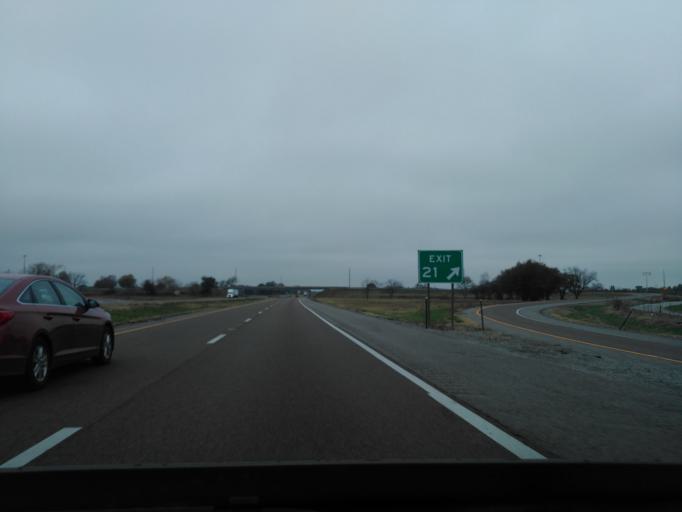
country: US
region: Illinois
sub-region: Madison County
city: Saint Jacob
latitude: 38.7622
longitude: -89.7964
